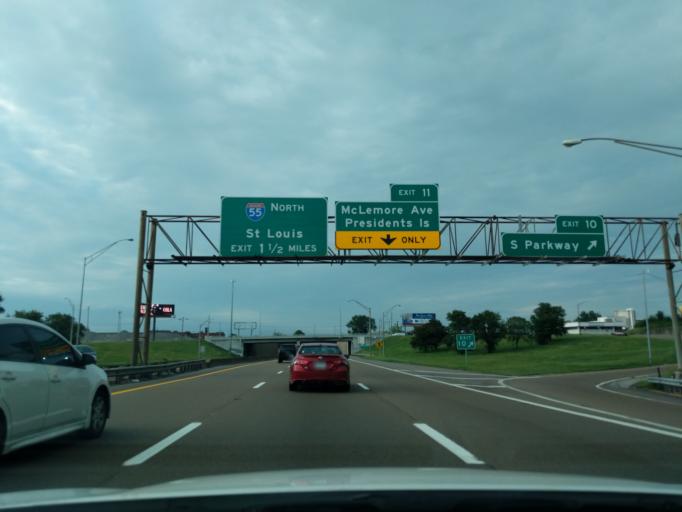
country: US
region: Tennessee
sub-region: Shelby County
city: New South Memphis
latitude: 35.1062
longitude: -90.0758
